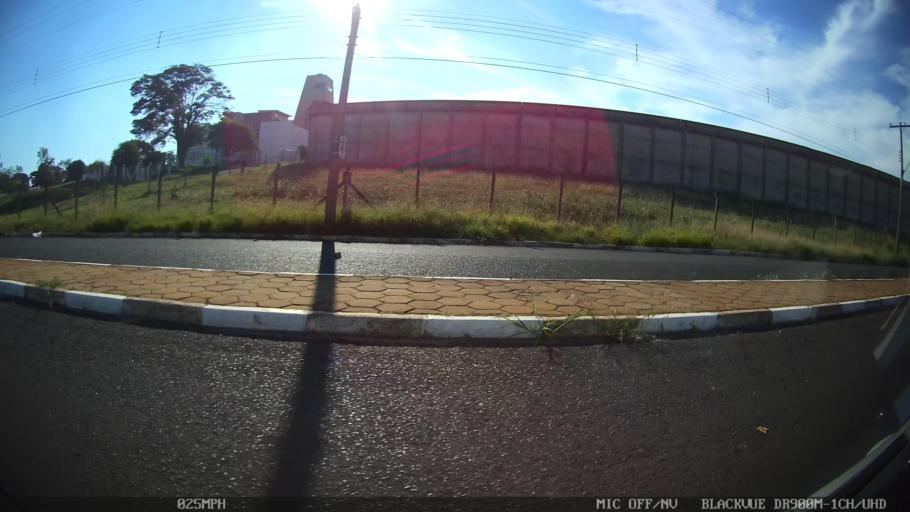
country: BR
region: Sao Paulo
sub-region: Araraquara
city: Araraquara
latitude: -21.7656
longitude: -48.1386
